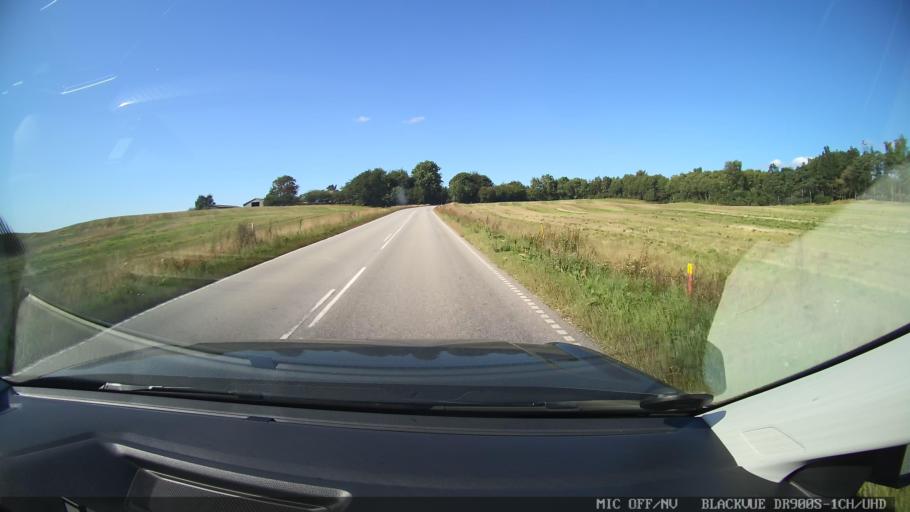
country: DK
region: North Denmark
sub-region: Mariagerfjord Kommune
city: Mariager
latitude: 56.6220
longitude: 9.9803
